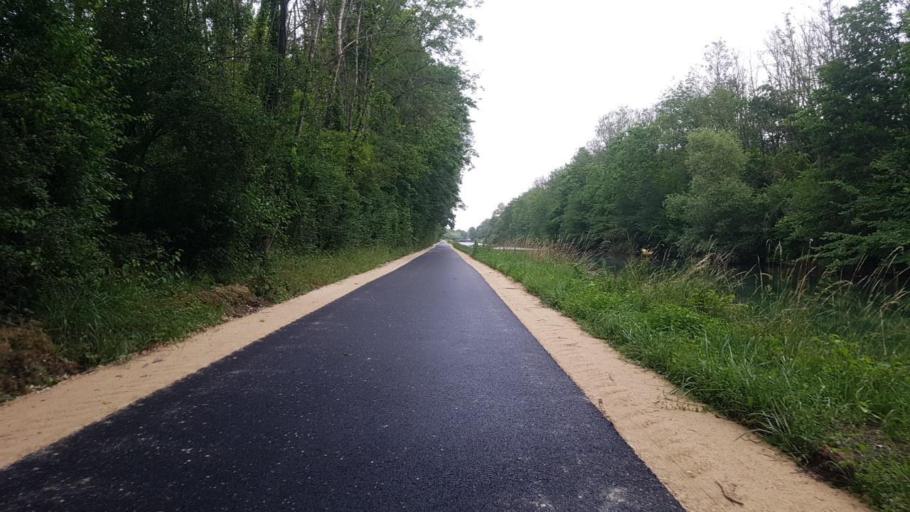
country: FR
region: Champagne-Ardenne
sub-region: Departement de la Marne
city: Vitry-le-Francois
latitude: 48.8032
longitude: 4.5229
